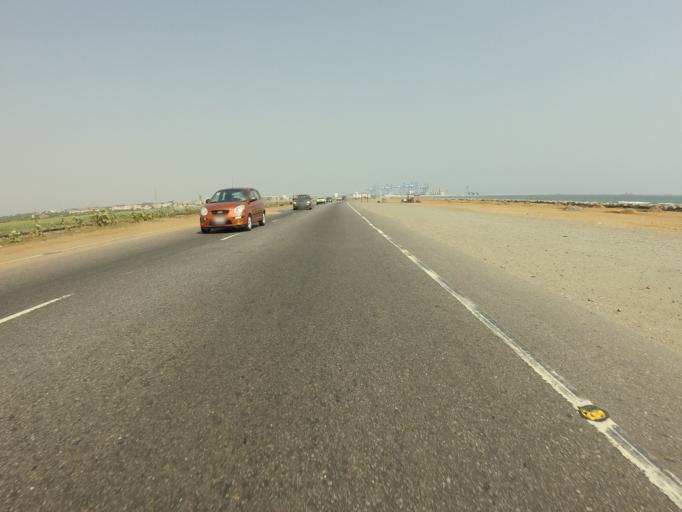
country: GH
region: Greater Accra
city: Nungua
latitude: 5.6134
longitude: -0.0347
